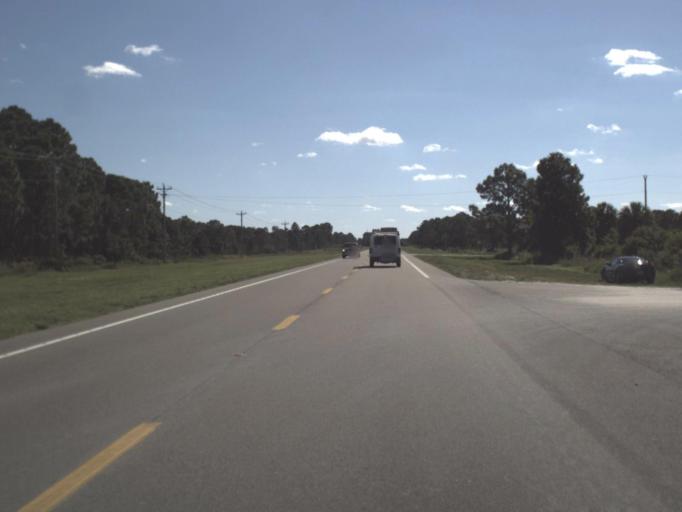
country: US
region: Florida
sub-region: Lee County
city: Lehigh Acres
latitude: 26.5227
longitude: -81.5804
